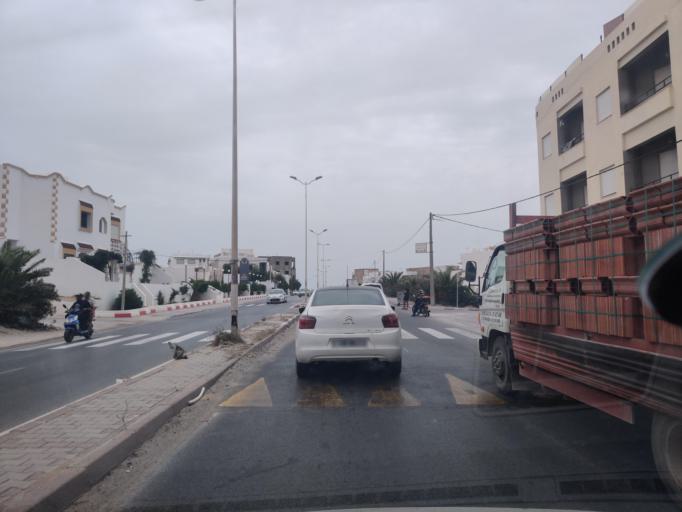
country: TN
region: Nabul
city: Al Hammamat
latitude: 36.4087
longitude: 10.6277
